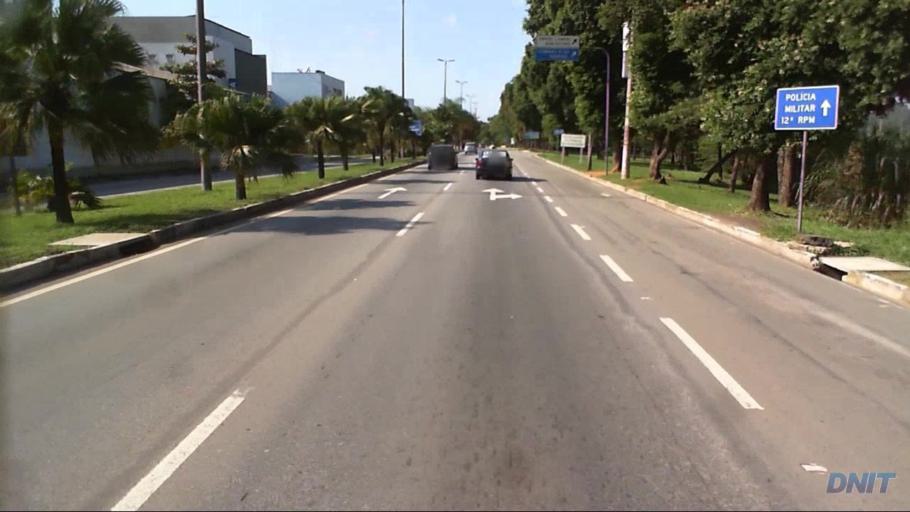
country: BR
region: Minas Gerais
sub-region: Ipatinga
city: Ipatinga
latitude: -19.5084
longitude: -42.5718
